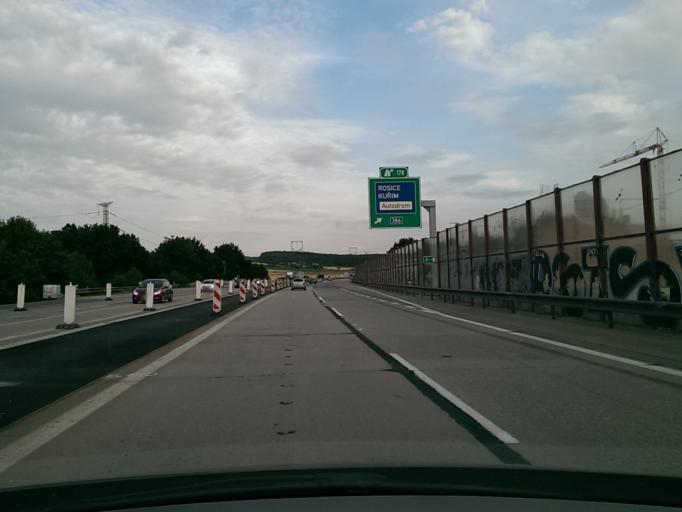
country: CZ
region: South Moravian
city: Ricany
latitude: 49.2171
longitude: 16.4089
